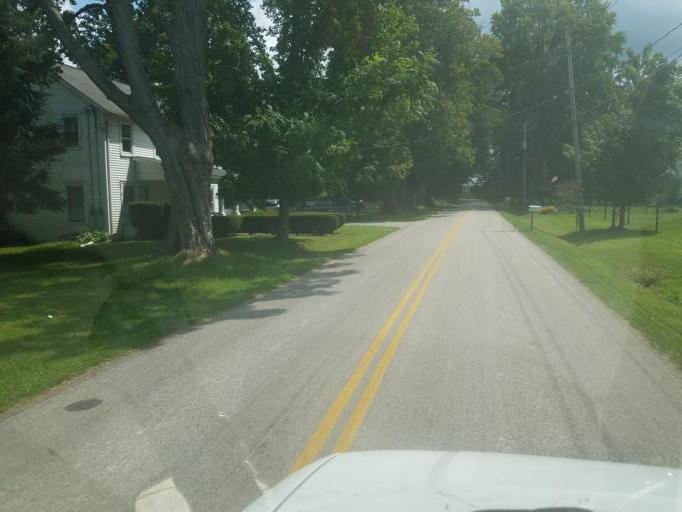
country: US
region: Ohio
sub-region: Ashtabula County
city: Roaming Shores
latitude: 41.5869
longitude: -80.8095
